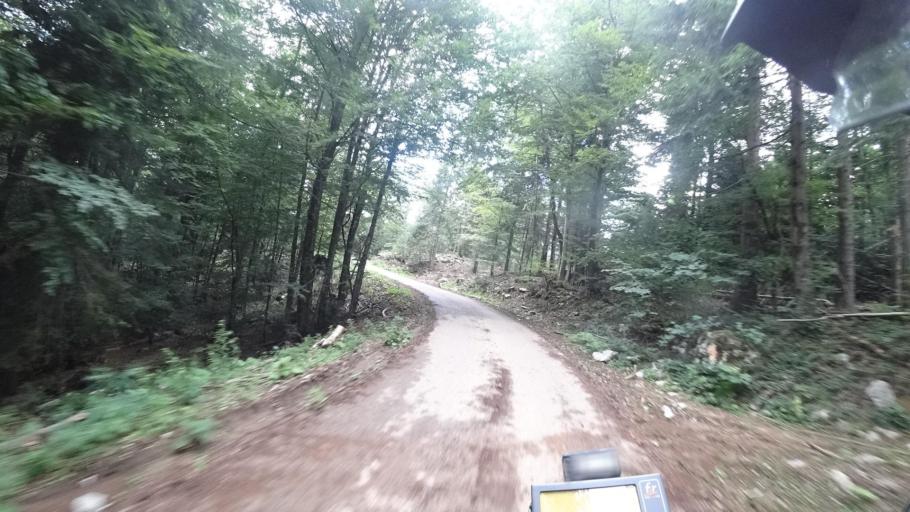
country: HR
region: Licko-Senjska
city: Senj
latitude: 45.0923
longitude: 14.9552
